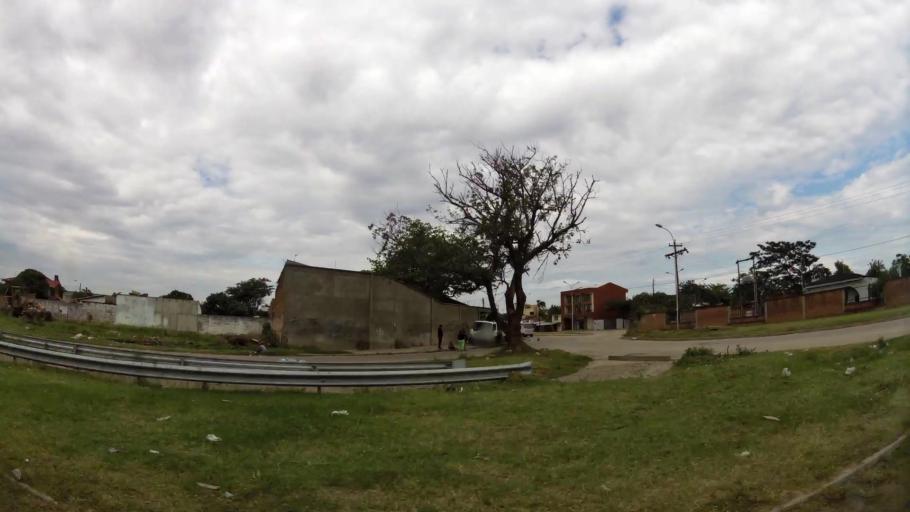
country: BO
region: Santa Cruz
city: Santa Cruz de la Sierra
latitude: -17.7394
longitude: -63.1904
